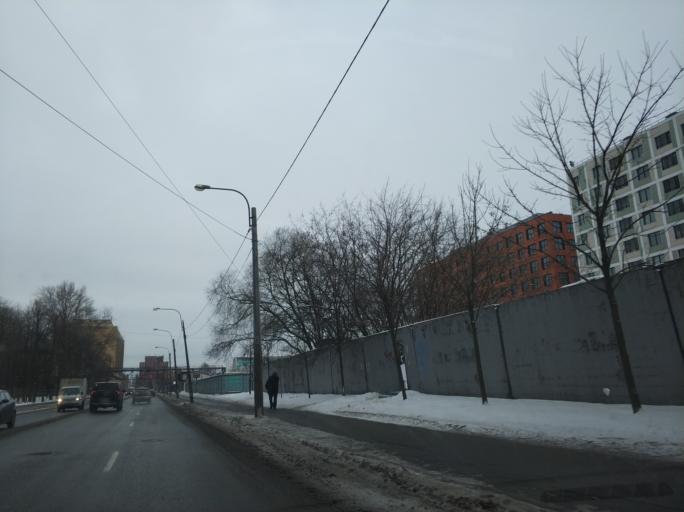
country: RU
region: St.-Petersburg
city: Centralniy
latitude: 59.9210
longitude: 30.3731
